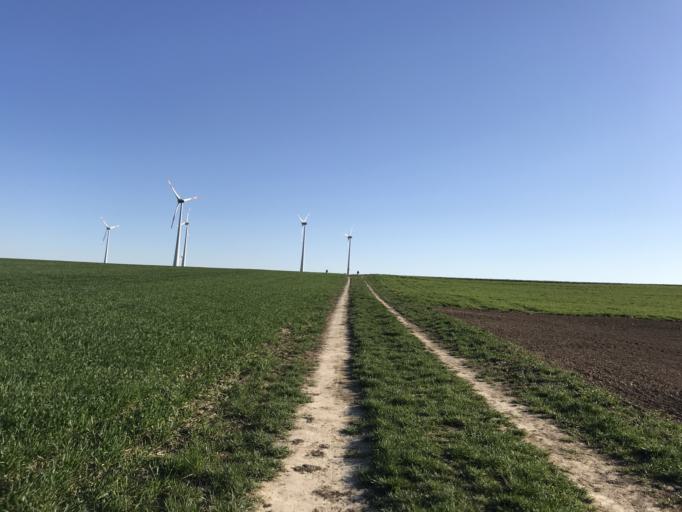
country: DE
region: Rheinland-Pfalz
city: Klein-Winternheim
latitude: 49.9489
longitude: 8.2341
